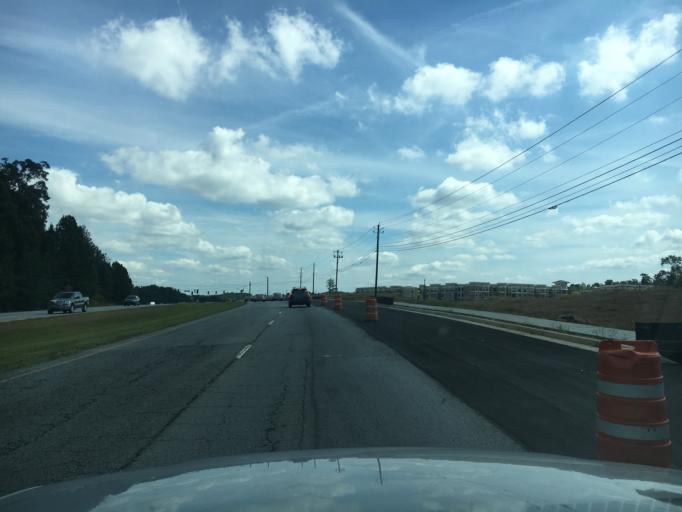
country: US
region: Georgia
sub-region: Gwinnett County
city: Duluth
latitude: 34.0213
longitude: -84.1267
